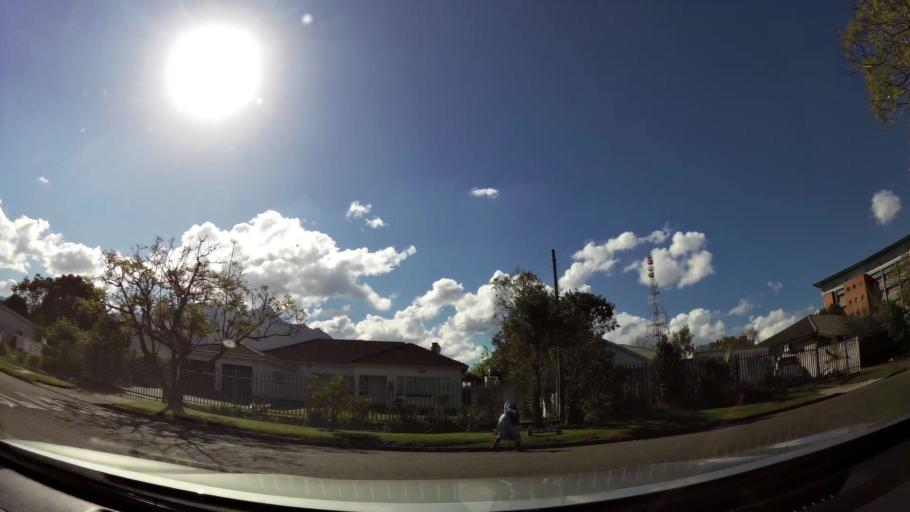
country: ZA
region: Western Cape
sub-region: Eden District Municipality
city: George
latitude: -33.9609
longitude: 22.4522
